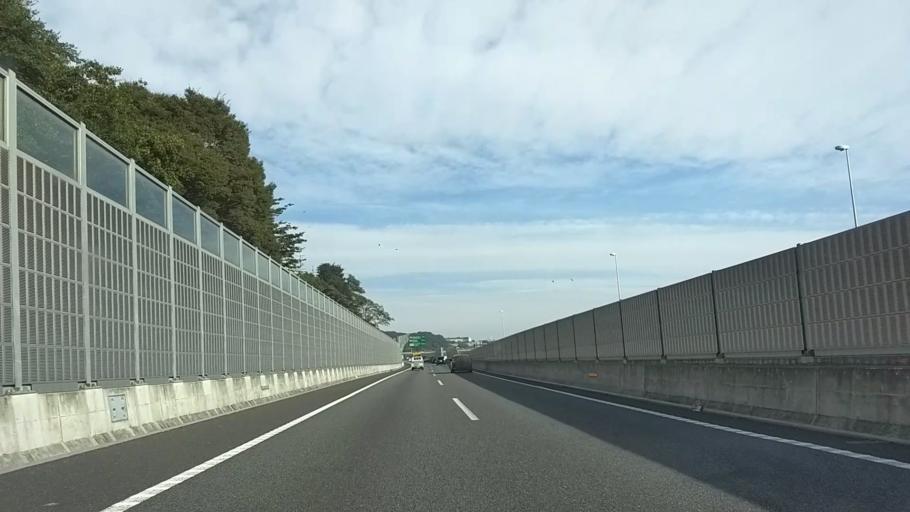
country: JP
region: Kanagawa
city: Zama
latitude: 35.4929
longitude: 139.3681
